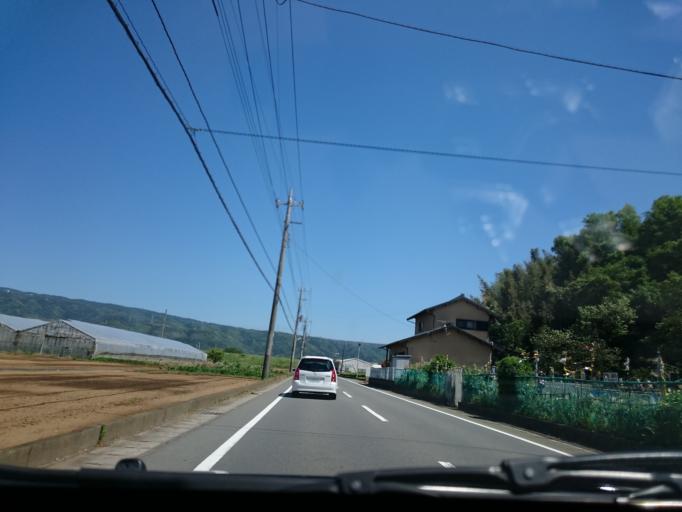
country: JP
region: Shizuoka
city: Mishima
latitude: 35.0676
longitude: 138.9336
